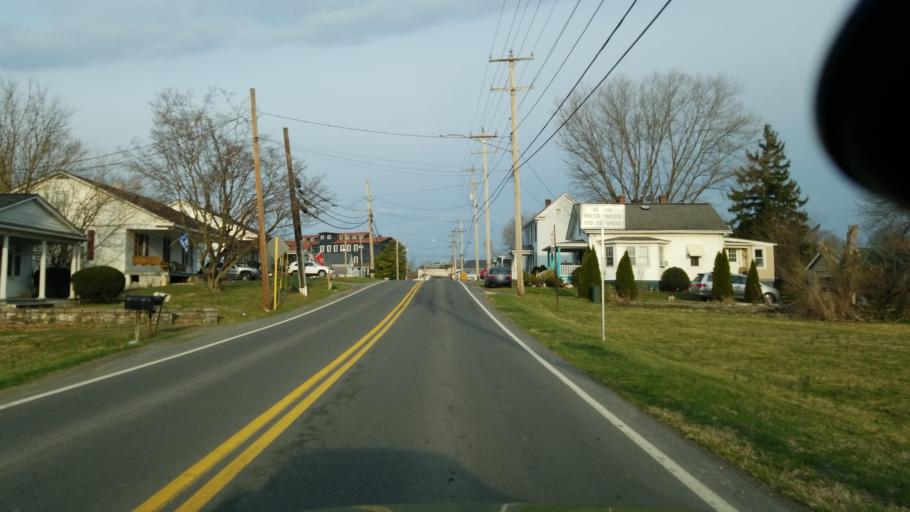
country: US
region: Virginia
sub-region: Clarke County
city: Berryville
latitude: 39.1473
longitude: -77.9728
